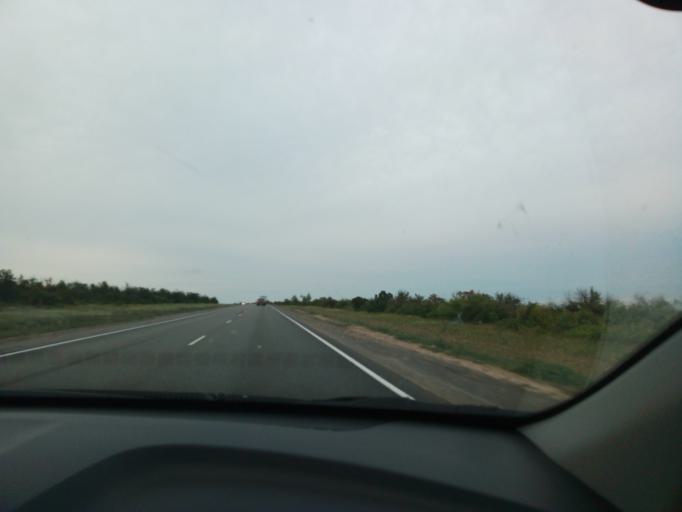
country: RU
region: Volgograd
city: Primorsk
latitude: 49.2057
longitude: 44.8983
